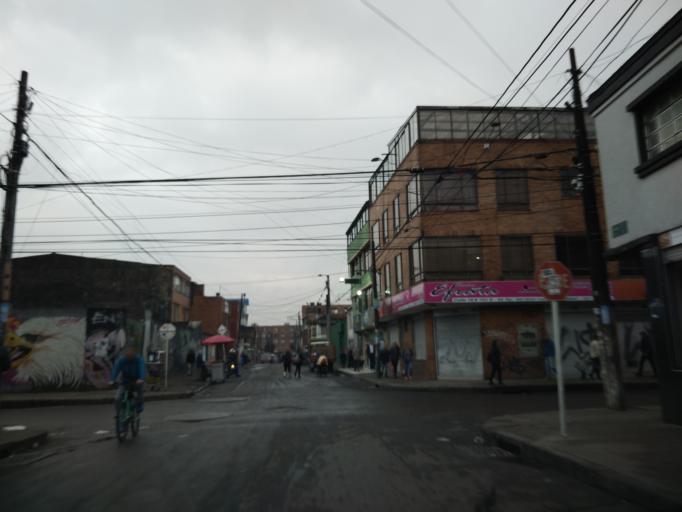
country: CO
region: Cundinamarca
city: Funza
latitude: 4.6766
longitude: -74.1470
